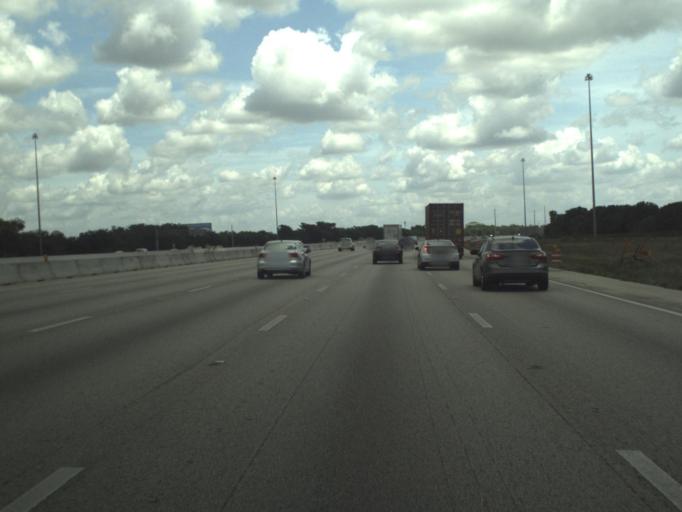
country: US
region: Florida
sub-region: Broward County
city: Weston
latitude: 26.0905
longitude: -80.3631
